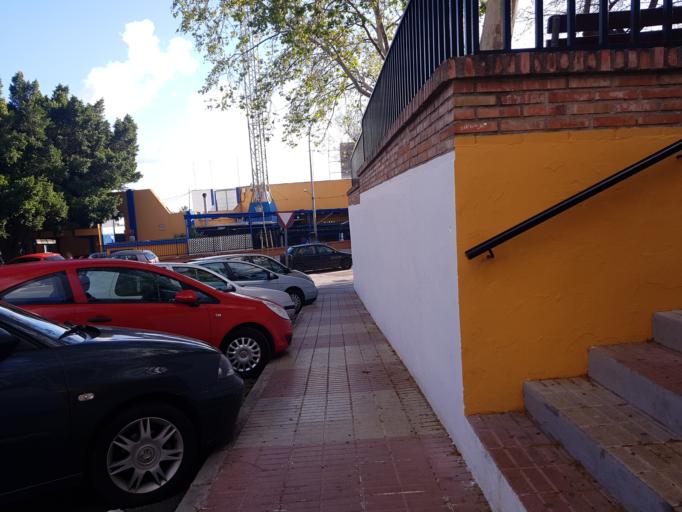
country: ES
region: Andalusia
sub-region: Provincia de Malaga
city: Marbella
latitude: 36.5129
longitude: -4.8783
